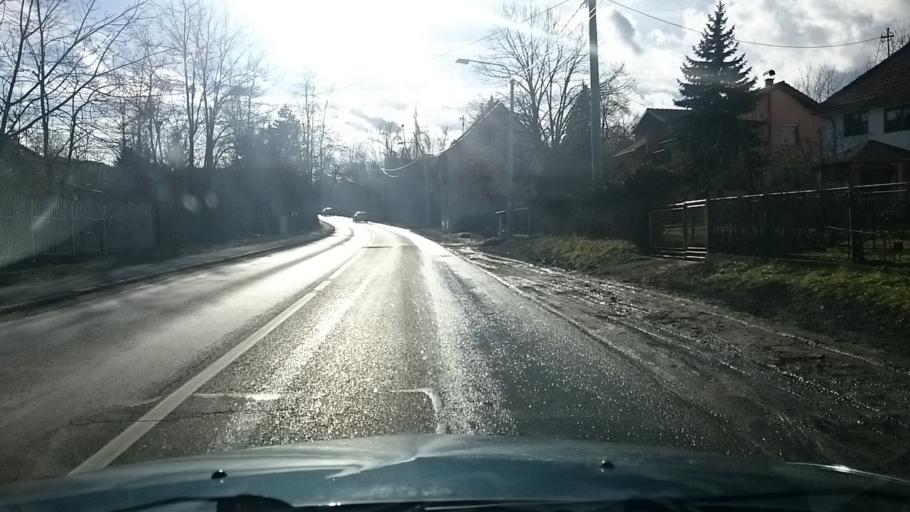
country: BA
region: Republika Srpska
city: Hiseti
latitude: 44.7656
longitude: 17.1774
